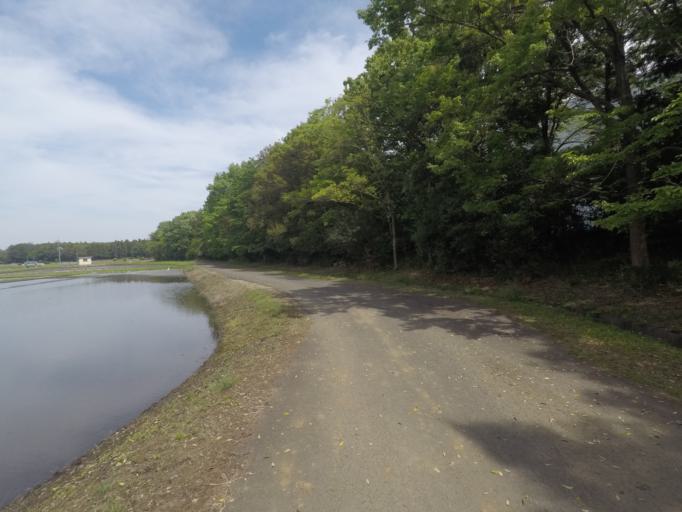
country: JP
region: Ibaraki
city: Ishige
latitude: 36.1164
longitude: 140.0212
